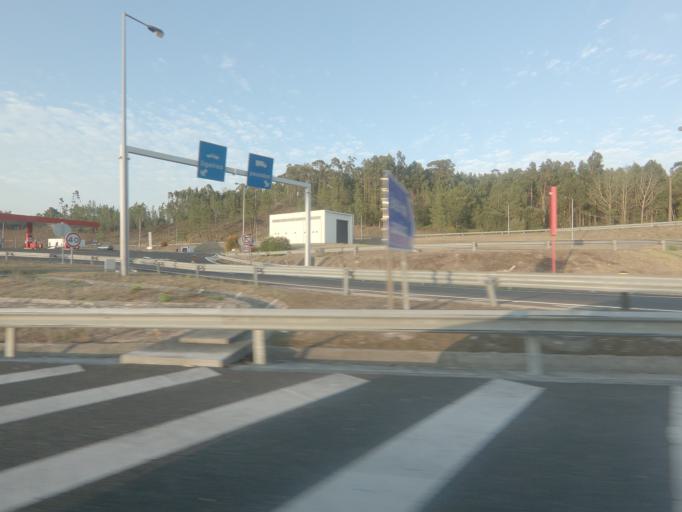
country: PT
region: Leiria
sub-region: Leiria
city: Caranguejeira
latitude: 39.7116
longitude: -8.7096
